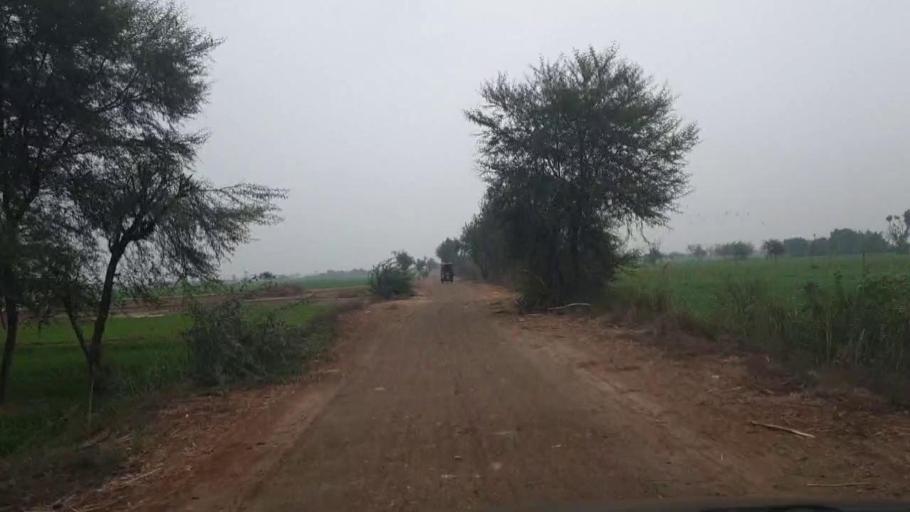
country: PK
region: Sindh
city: Tando Adam
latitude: 25.8361
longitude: 68.6873
